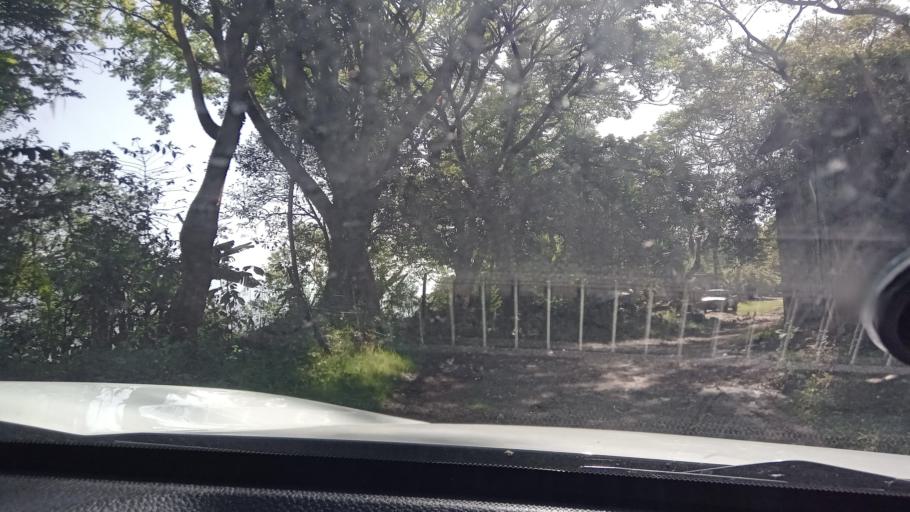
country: MX
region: Veracruz
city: El Castillo
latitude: 19.5661
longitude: -96.8657
